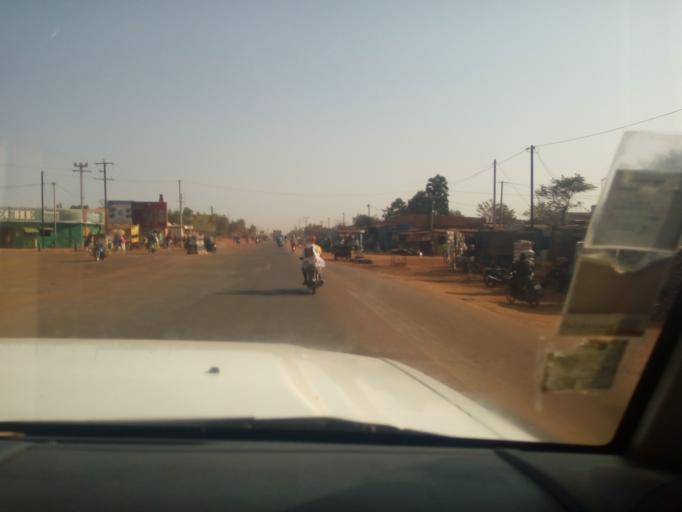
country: BF
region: Centre
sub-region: Kadiogo Province
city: Ouagadougou
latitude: 12.4153
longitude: -1.4758
